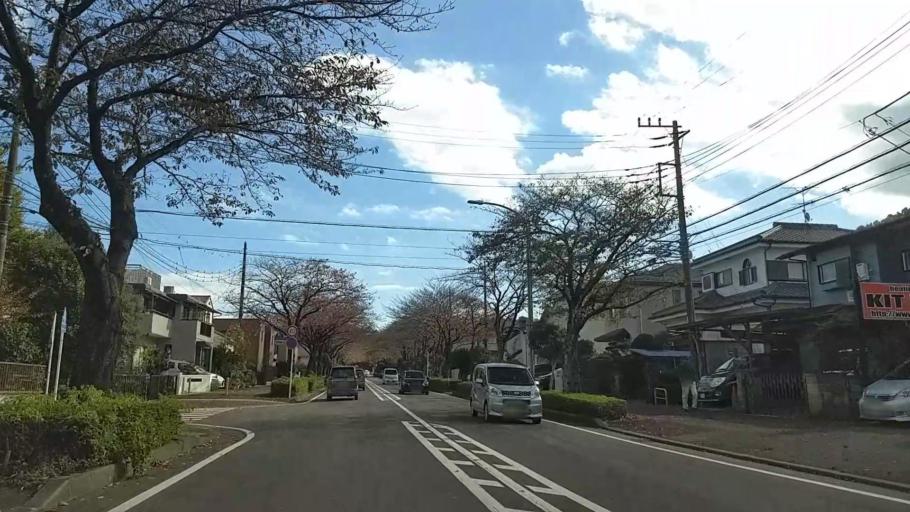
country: JP
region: Kanagawa
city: Hadano
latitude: 35.3647
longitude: 139.2130
